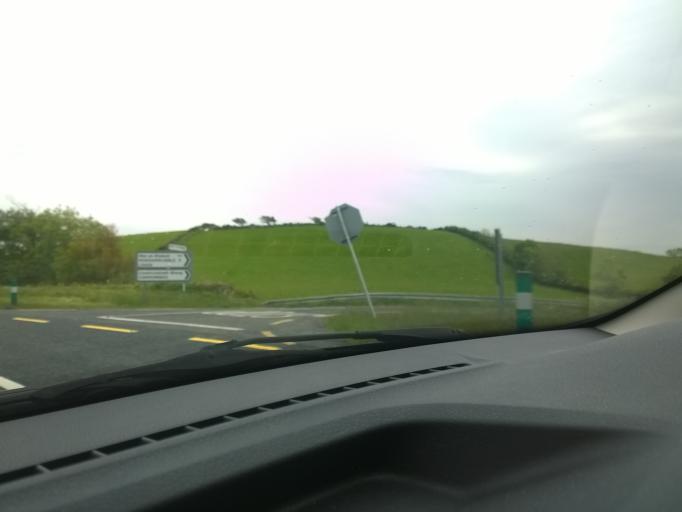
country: IE
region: Connaught
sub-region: Maigh Eo
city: Westport
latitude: 53.8754
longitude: -9.5421
